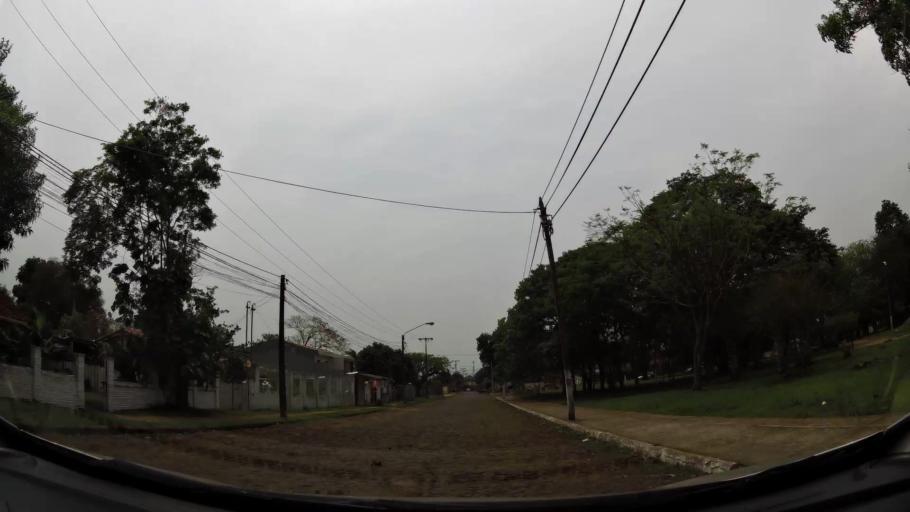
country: PY
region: Alto Parana
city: Presidente Franco
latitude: -25.5528
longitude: -54.6266
